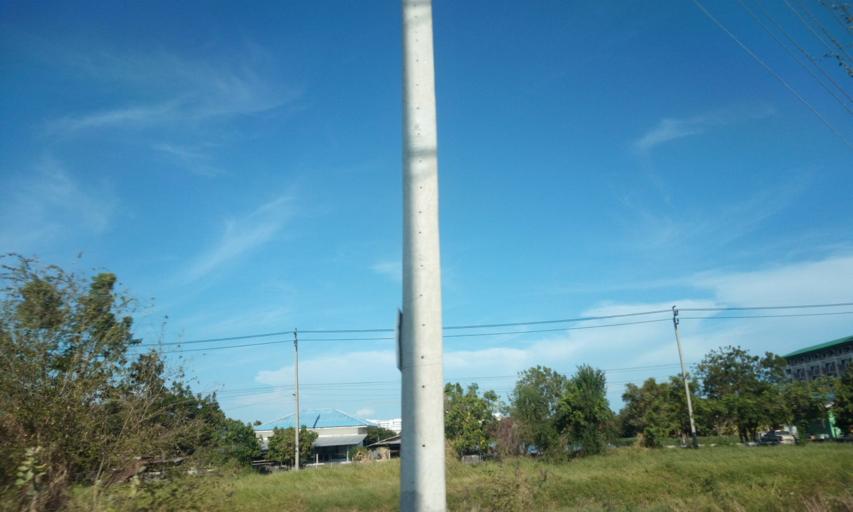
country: TH
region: Samut Prakan
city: Bang Bo District
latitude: 13.5275
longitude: 100.7491
